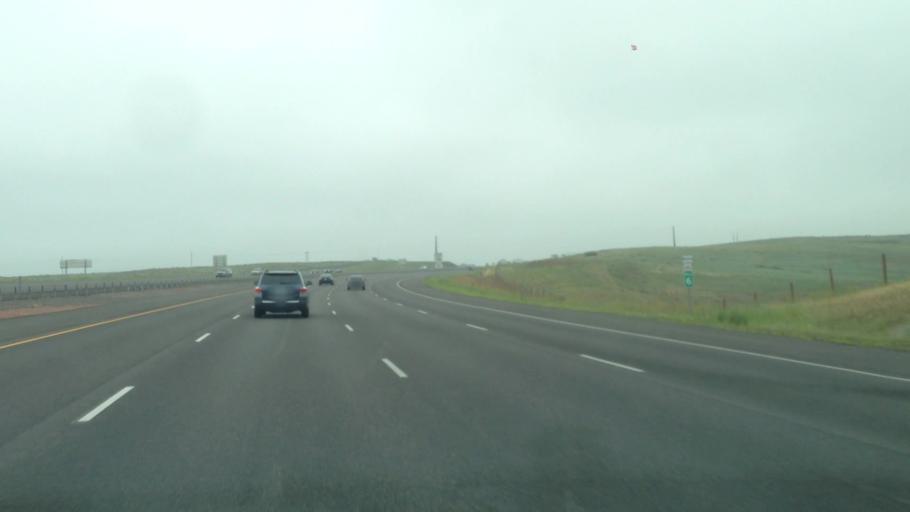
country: US
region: Colorado
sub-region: Douglas County
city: Parker
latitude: 39.5604
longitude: -104.7703
